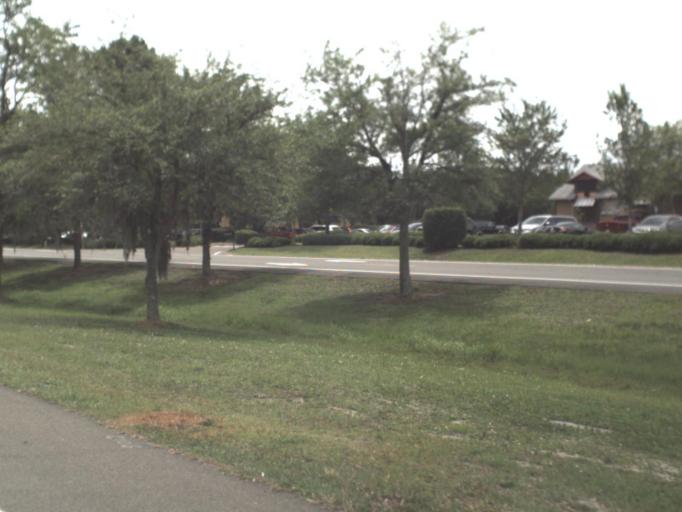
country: US
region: Florida
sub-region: Duval County
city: Jacksonville
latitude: 30.4832
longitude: -81.6546
